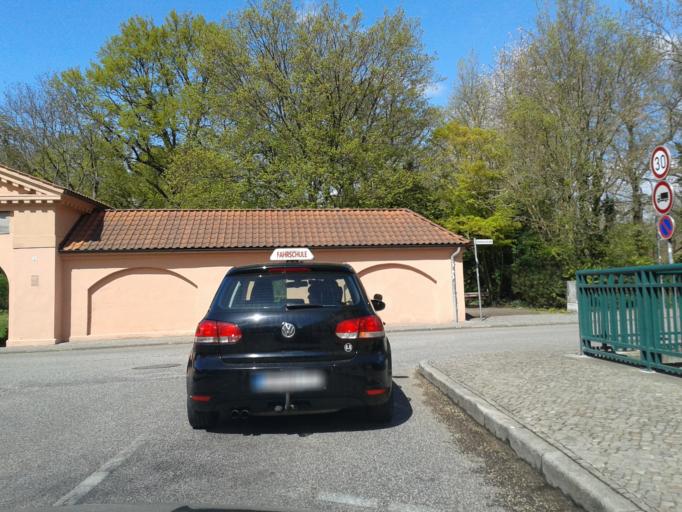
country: DE
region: Saxony-Anhalt
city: Salzwedel
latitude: 52.8543
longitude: 11.1516
